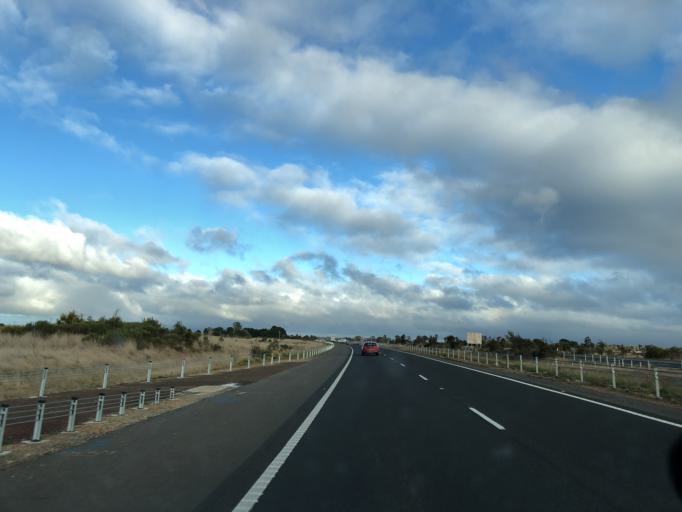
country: AU
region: Victoria
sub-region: Mount Alexander
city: Castlemaine
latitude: -37.2018
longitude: 144.4072
